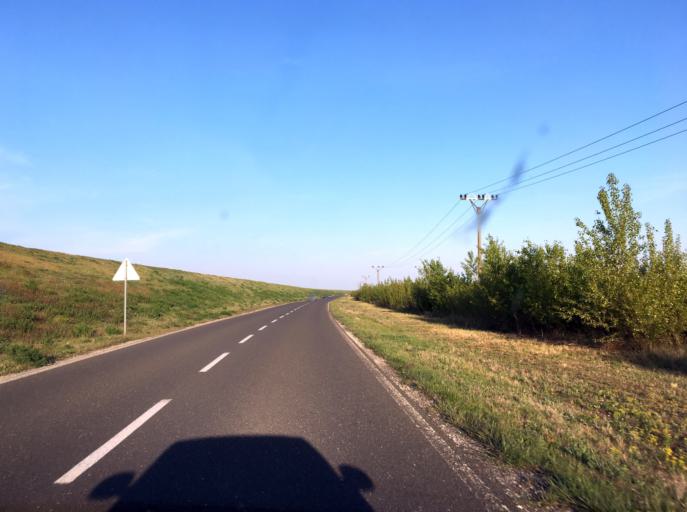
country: SK
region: Trnavsky
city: Samorin
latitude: 47.9978
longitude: 17.3217
